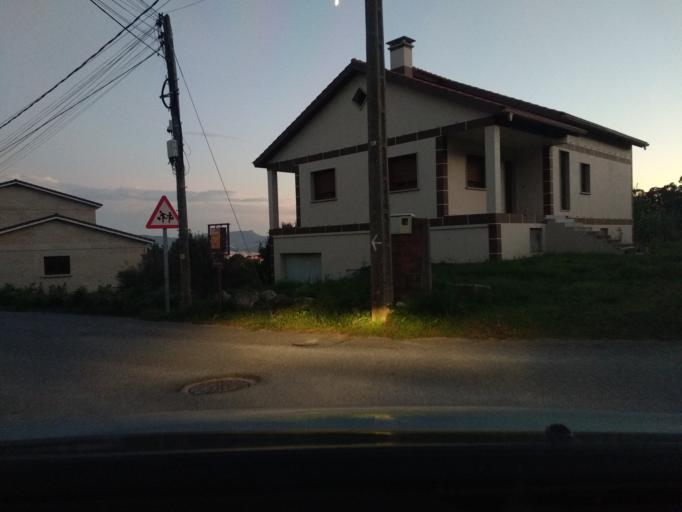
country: ES
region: Galicia
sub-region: Provincia de Pontevedra
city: Moana
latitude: 42.2868
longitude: -8.7510
